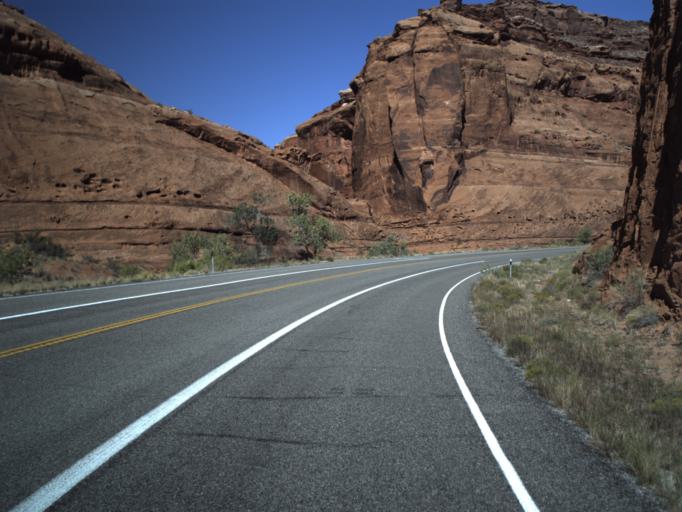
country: US
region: Utah
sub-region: San Juan County
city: Blanding
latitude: 37.9632
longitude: -110.4915
